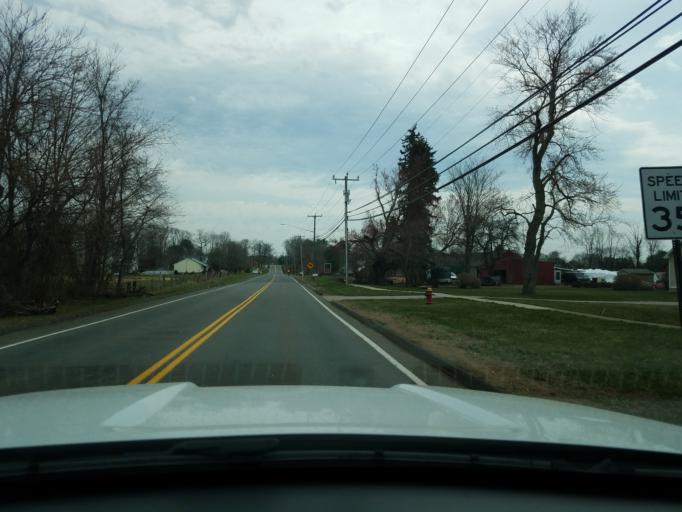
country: US
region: Connecticut
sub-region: Hartford County
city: Newington
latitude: 41.6646
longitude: -72.6870
